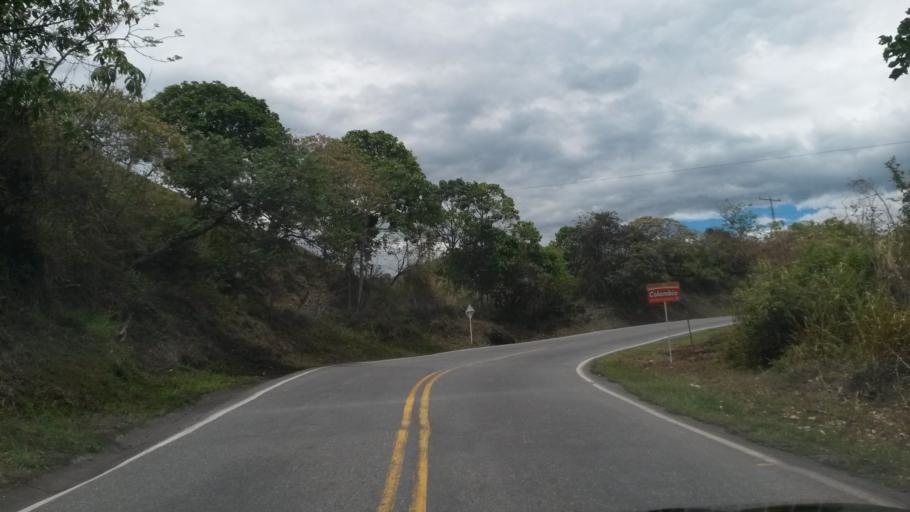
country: CO
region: Cauca
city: Rosas
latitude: 2.2542
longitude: -76.7604
